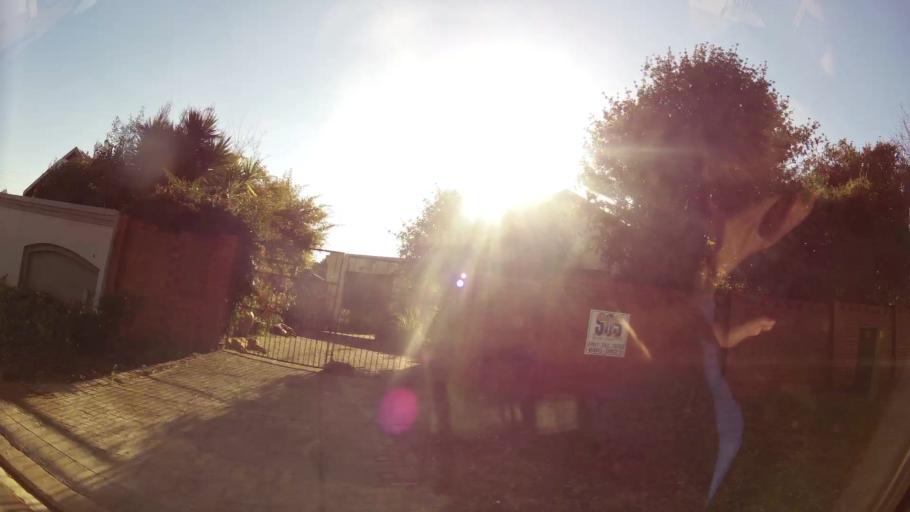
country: ZA
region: Gauteng
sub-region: City of Johannesburg Metropolitan Municipality
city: Johannesburg
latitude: -26.2919
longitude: 28.0503
